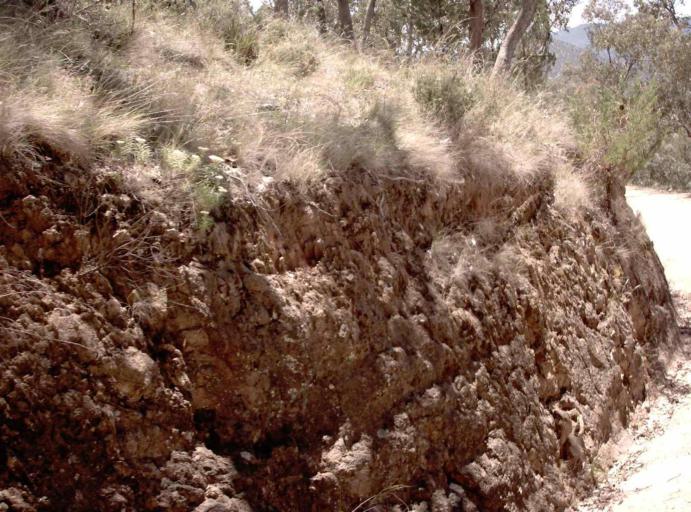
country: AU
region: New South Wales
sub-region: Snowy River
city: Jindabyne
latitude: -36.9301
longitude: 148.3700
